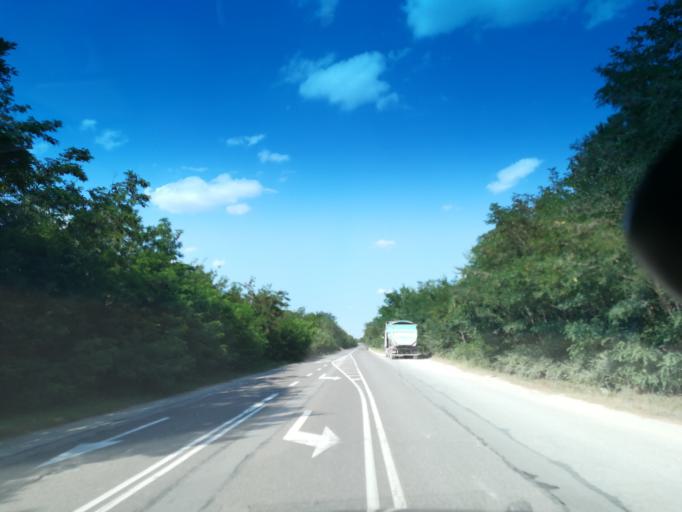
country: BG
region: Stara Zagora
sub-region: Obshtina Chirpan
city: Chirpan
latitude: 42.2413
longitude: 25.4040
